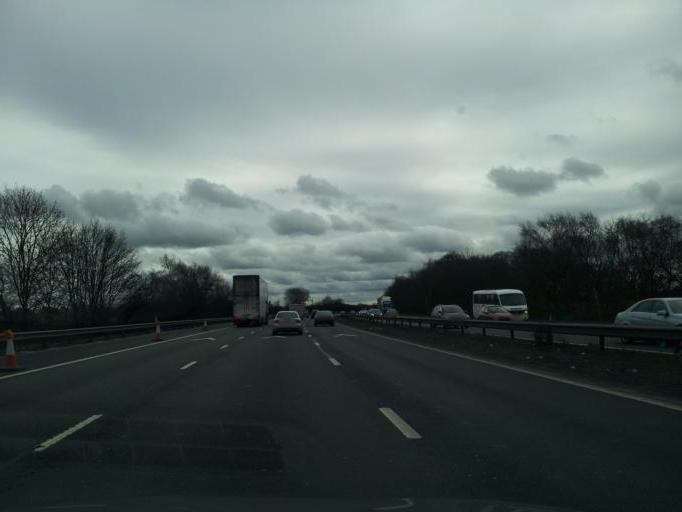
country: GB
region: England
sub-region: Staffordshire
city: Barlaston
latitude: 52.9127
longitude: -2.1942
